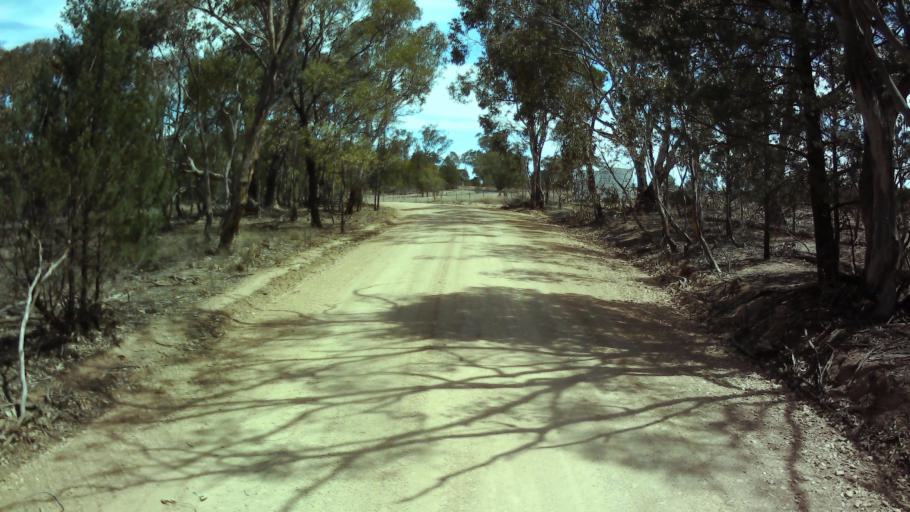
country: AU
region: New South Wales
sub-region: Weddin
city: Grenfell
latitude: -33.8095
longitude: 148.1580
